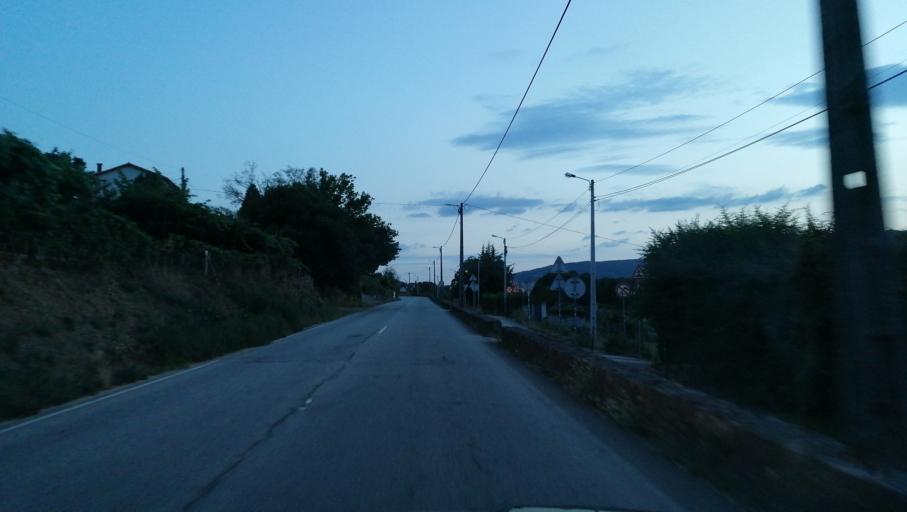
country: PT
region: Vila Real
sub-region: Vila Pouca de Aguiar
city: Vila Pouca de Aguiar
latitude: 41.5389
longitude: -7.6059
